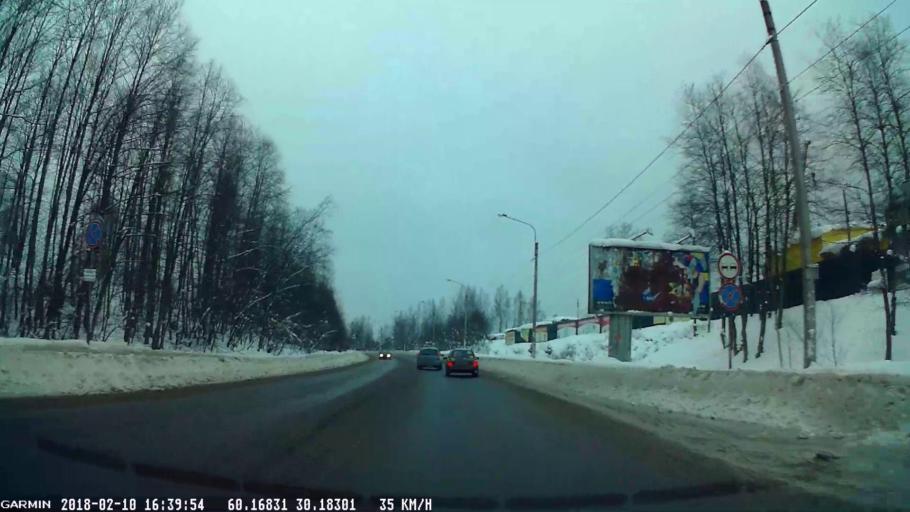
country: RU
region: Leningrad
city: Sertolovo
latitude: 60.1587
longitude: 30.1868
